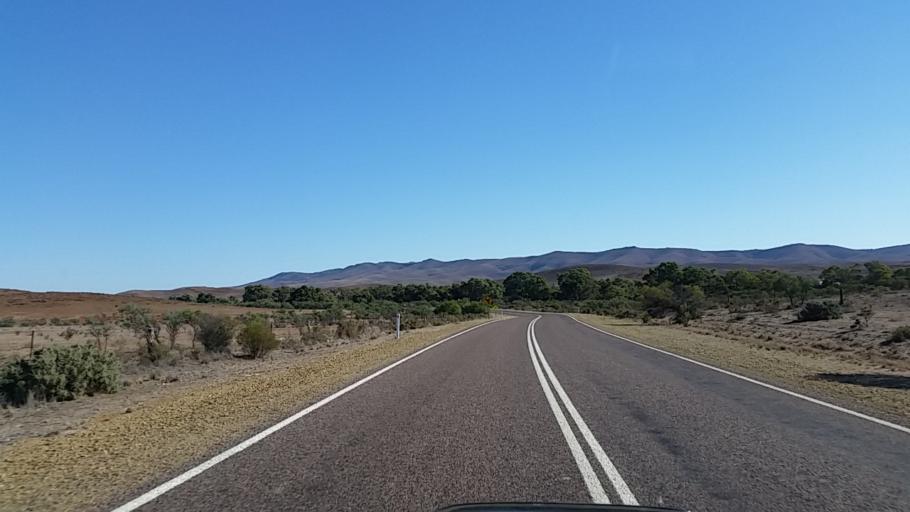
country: AU
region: South Australia
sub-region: Flinders Ranges
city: Quorn
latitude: -32.3276
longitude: 138.4769
